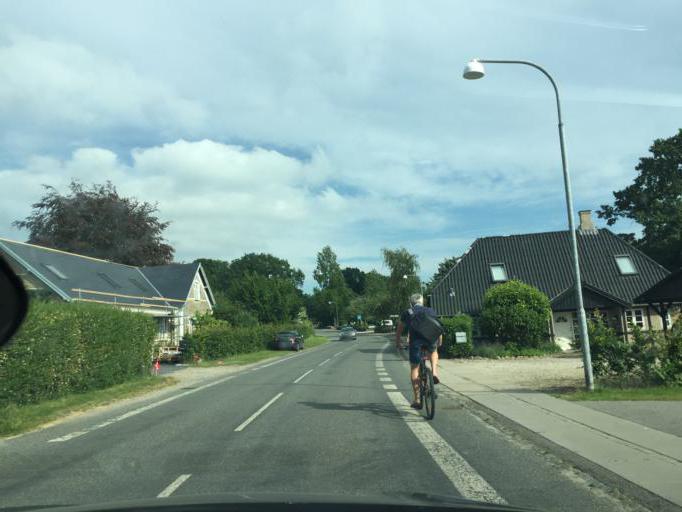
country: DK
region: South Denmark
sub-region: Faaborg-Midtfyn Kommune
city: Arslev
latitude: 55.3090
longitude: 10.4894
